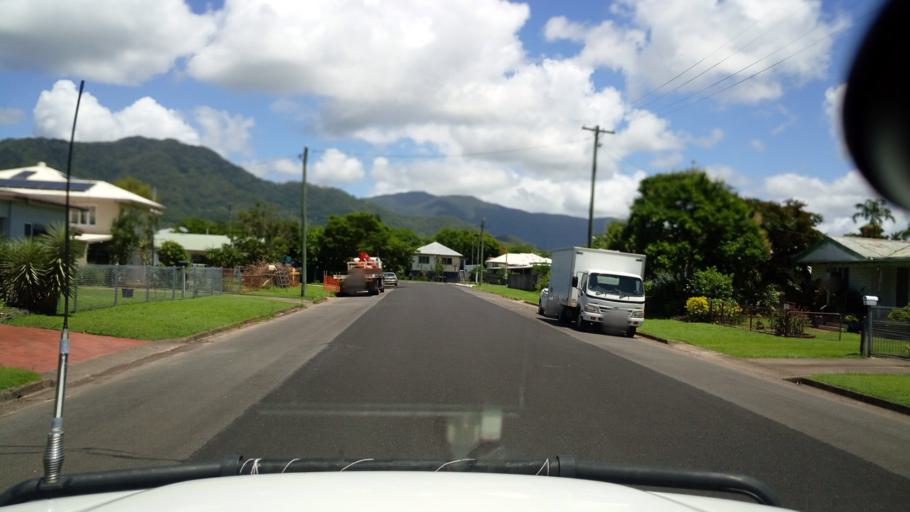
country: AU
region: Queensland
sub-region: Cairns
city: Cairns
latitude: -16.9219
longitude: 145.7475
